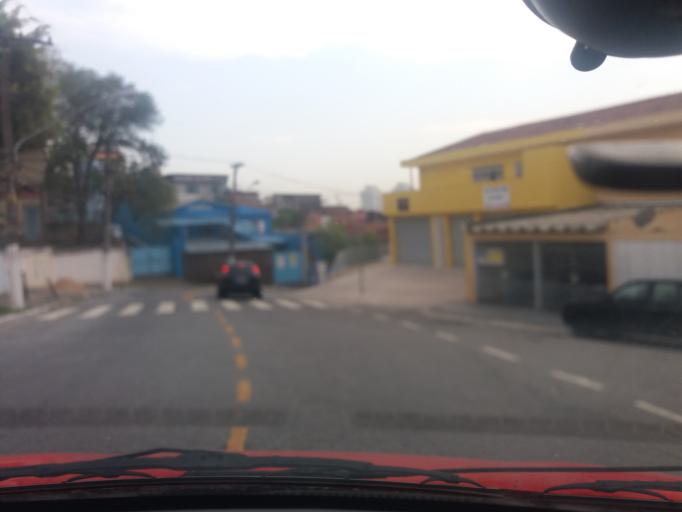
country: BR
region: Sao Paulo
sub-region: Taboao Da Serra
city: Taboao da Serra
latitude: -23.6187
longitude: -46.7457
